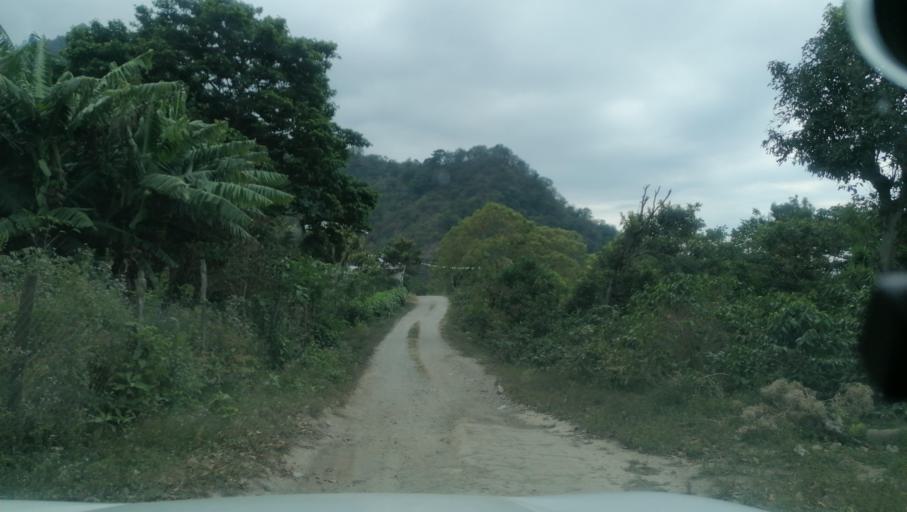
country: MX
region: Chiapas
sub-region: Cacahoatan
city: Benito Juarez
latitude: 15.1701
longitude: -92.1678
